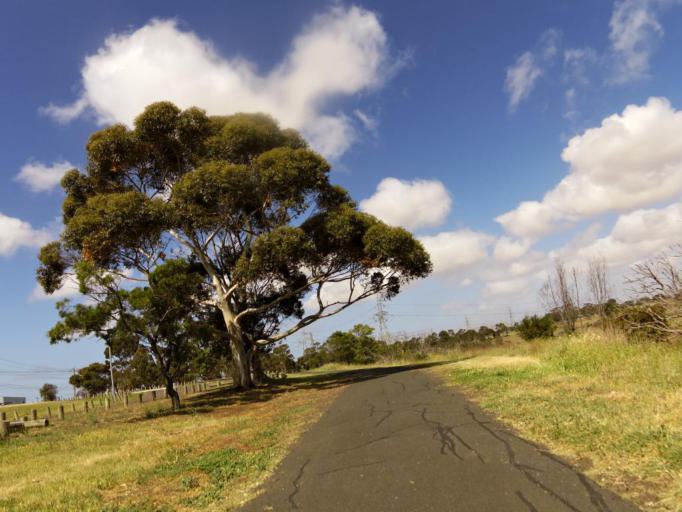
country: AU
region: Victoria
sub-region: Brimbank
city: Keilor Park
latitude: -37.7314
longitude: 144.8499
